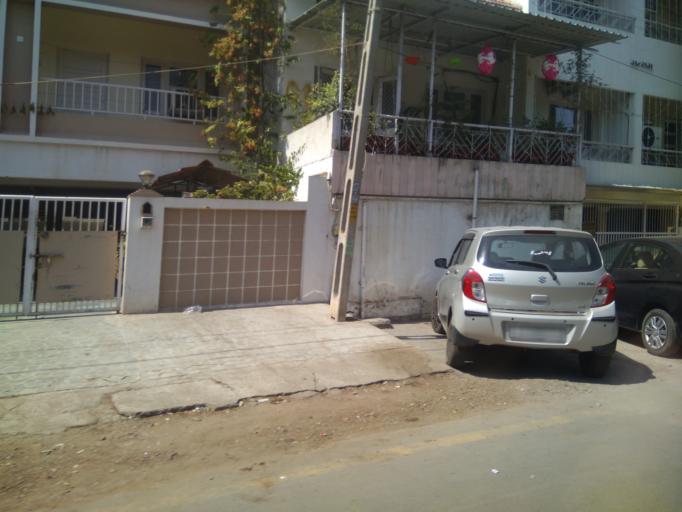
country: IN
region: Gujarat
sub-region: Jamnagar
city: Jamnagar
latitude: 22.4817
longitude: 70.0549
